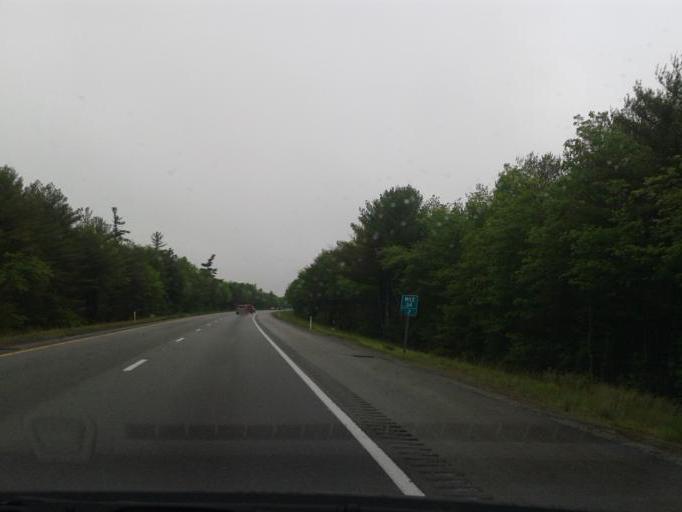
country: US
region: Massachusetts
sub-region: Plymouth County
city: Marion Center
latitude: 41.7145
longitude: -70.7878
